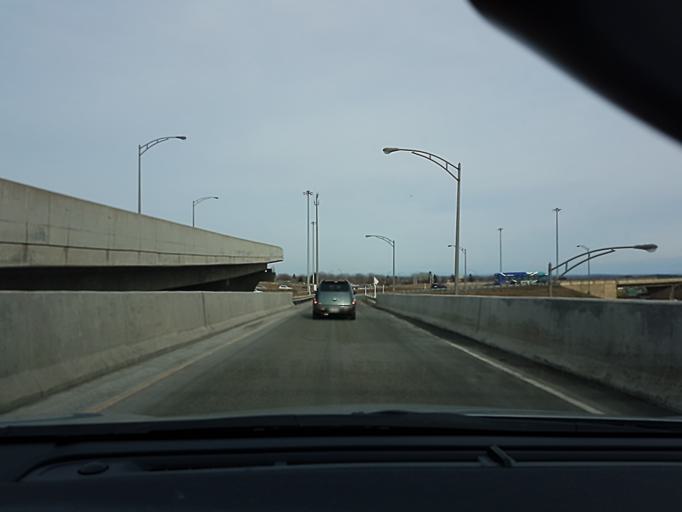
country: CA
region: Quebec
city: L'Ancienne-Lorette
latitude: 46.7612
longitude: -71.3011
